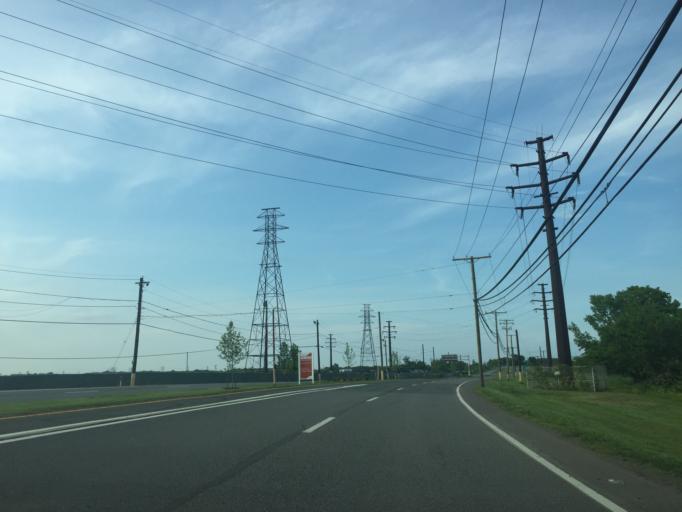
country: US
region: Maryland
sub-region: Baltimore County
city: Edgemere
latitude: 39.2261
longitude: -76.4688
